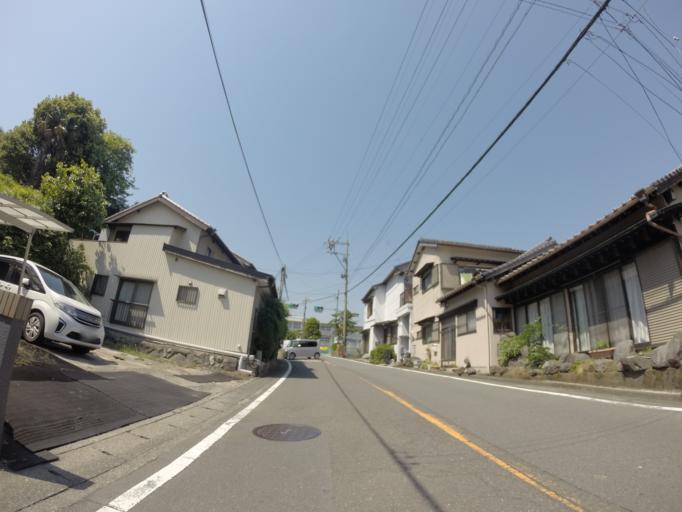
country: JP
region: Shizuoka
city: Fujinomiya
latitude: 35.1282
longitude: 138.5567
